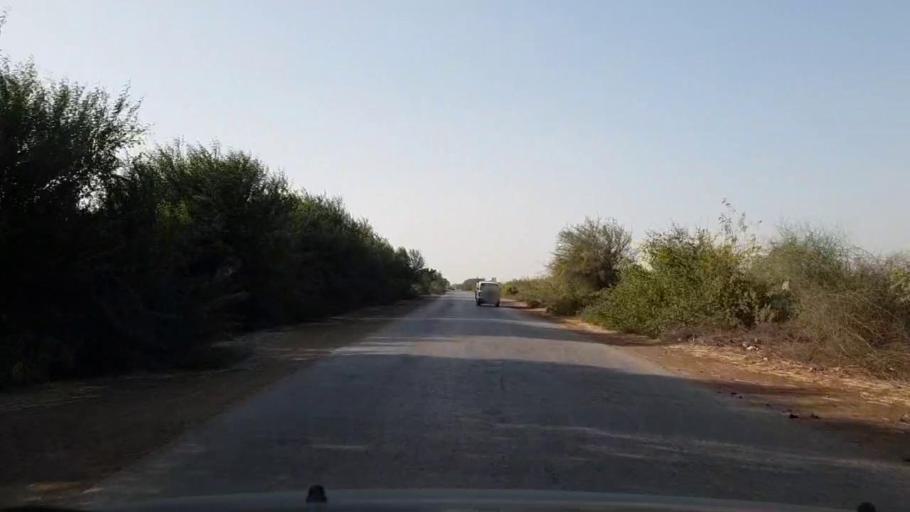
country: PK
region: Sindh
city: Tando Ghulam Ali
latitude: 25.1901
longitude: 68.8094
